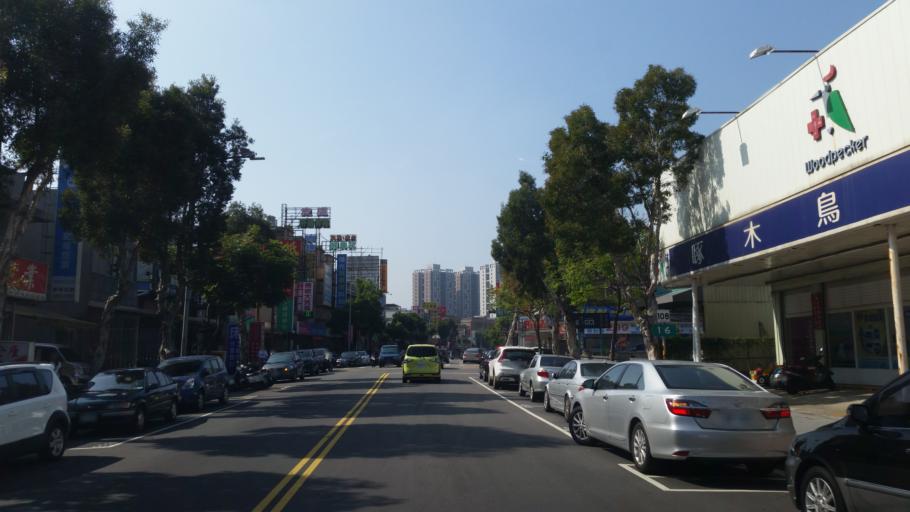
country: TW
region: Taipei
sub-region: Taipei
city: Banqiao
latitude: 25.0755
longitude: 121.3844
